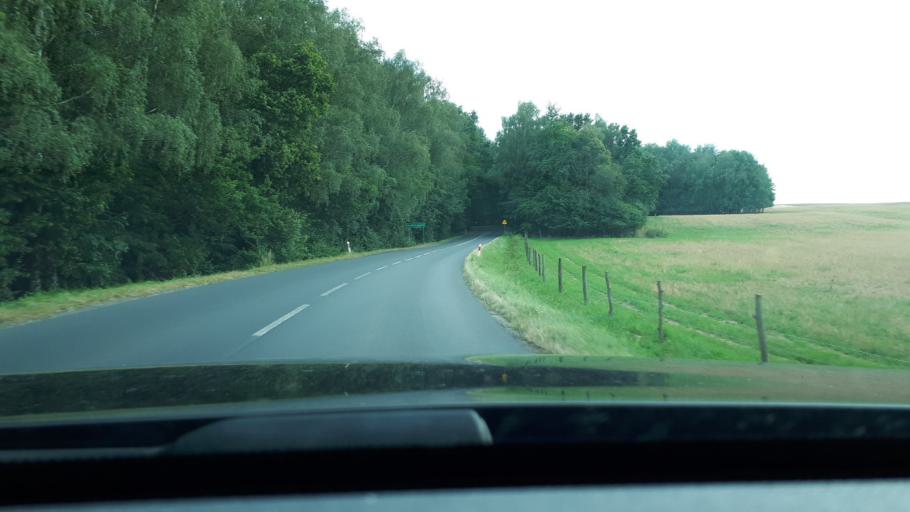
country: PL
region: Lower Silesian Voivodeship
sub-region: Powiat lubanski
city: Pisarzowice
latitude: 51.1565
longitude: 15.2668
